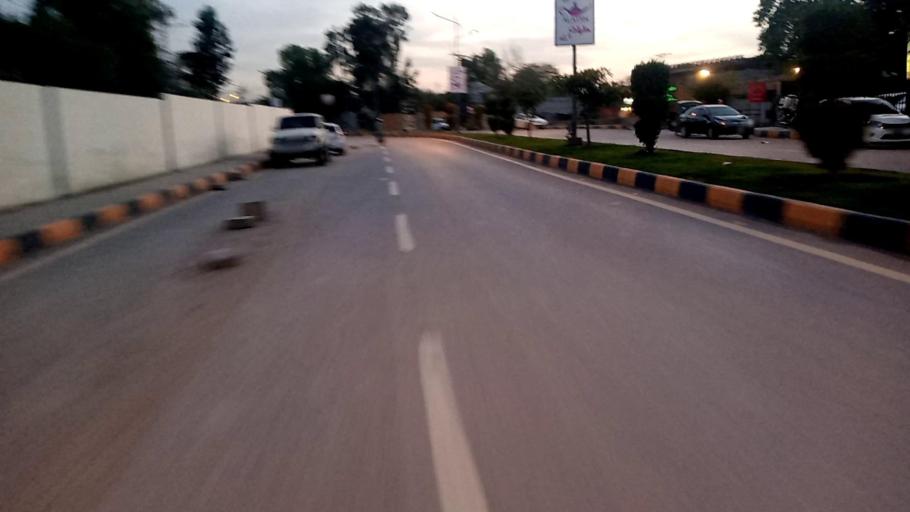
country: PK
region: Khyber Pakhtunkhwa
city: Peshawar
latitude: 34.0180
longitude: 71.5487
